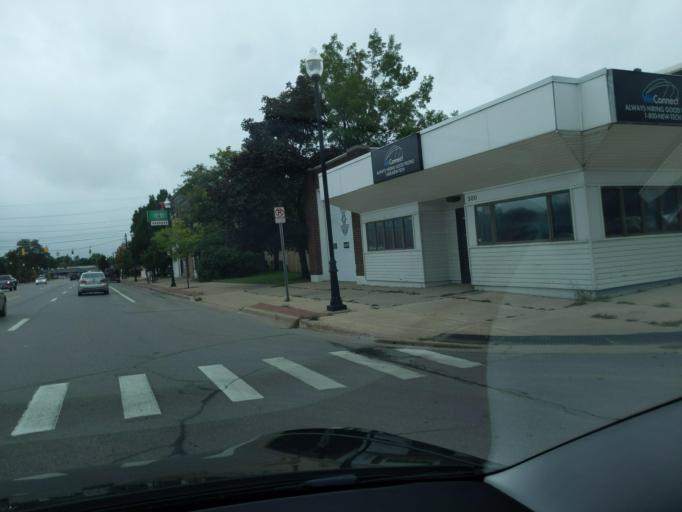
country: US
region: Michigan
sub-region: Wexford County
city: Cadillac
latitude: 44.2539
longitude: -85.4023
